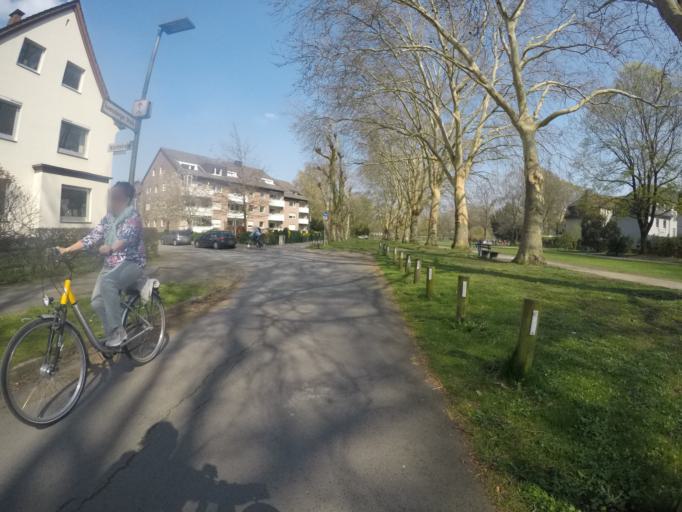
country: DE
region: North Rhine-Westphalia
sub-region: Regierungsbezirk Detmold
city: Bielefeld
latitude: 52.0201
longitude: 8.5558
